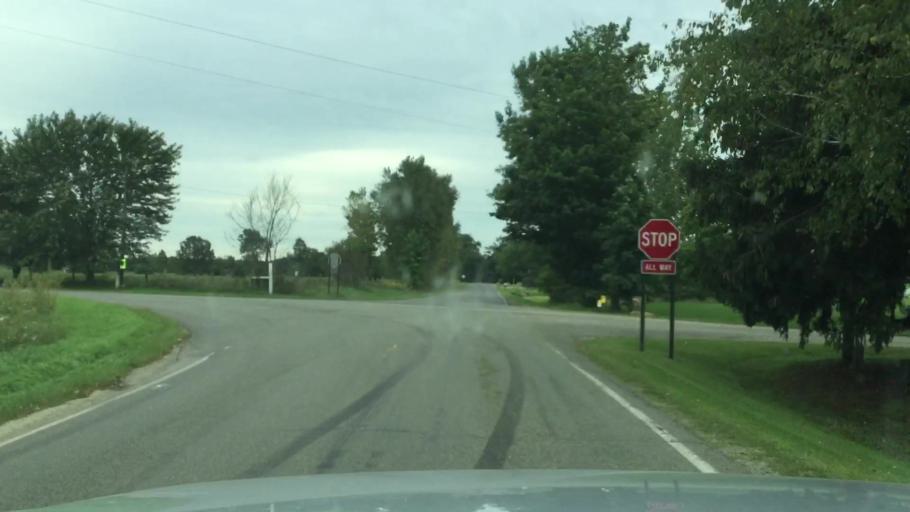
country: US
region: Michigan
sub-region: Shiawassee County
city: Durand
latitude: 42.8229
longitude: -84.0100
